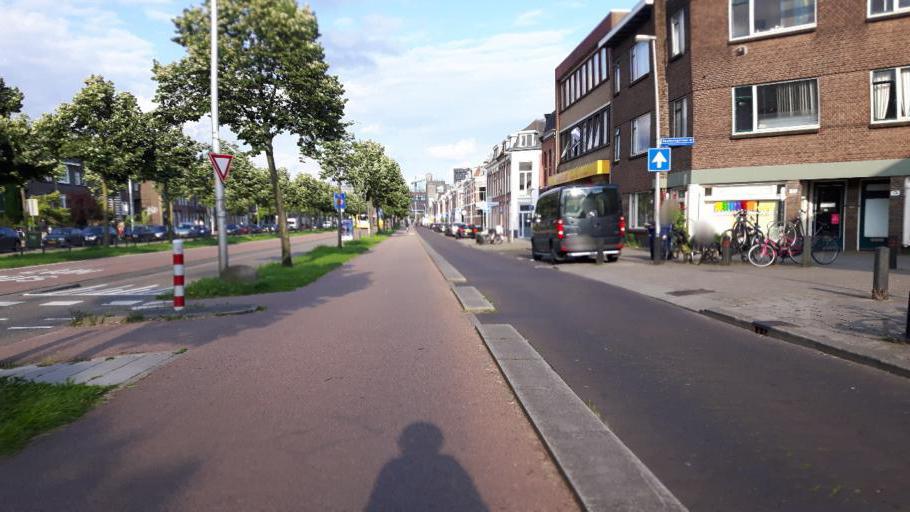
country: NL
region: Utrecht
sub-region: Gemeente Utrecht
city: Utrecht
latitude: 52.0931
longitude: 5.0987
